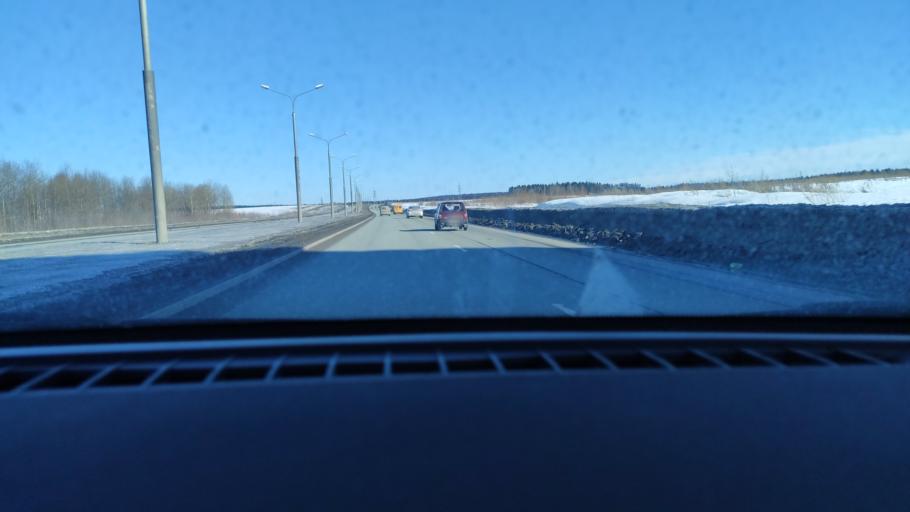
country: RU
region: Perm
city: Perm
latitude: 58.0059
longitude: 56.3390
